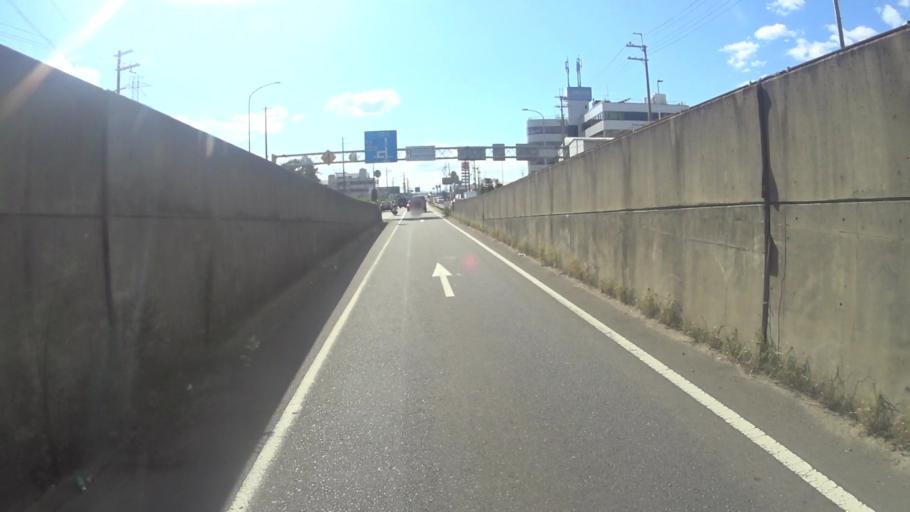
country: JP
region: Kyoto
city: Tanabe
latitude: 34.8469
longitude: 135.7833
